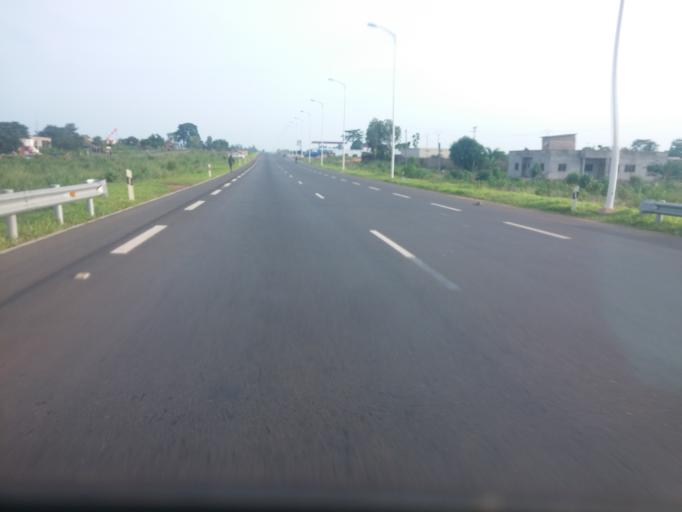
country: TG
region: Maritime
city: Tsevie
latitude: 6.3471
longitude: 1.2130
